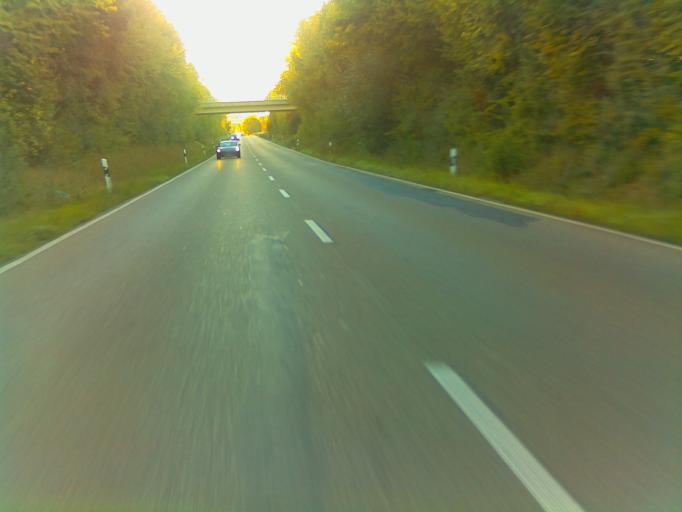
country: DE
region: Hesse
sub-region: Regierungsbezirk Darmstadt
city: Bad Homburg vor der Hoehe
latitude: 50.2110
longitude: 8.6381
